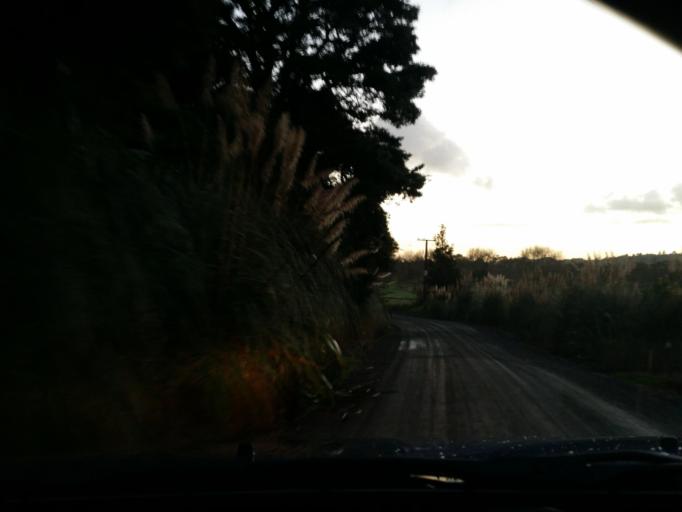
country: NZ
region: Northland
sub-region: Whangarei
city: Maungatapere
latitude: -35.8199
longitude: 174.0398
